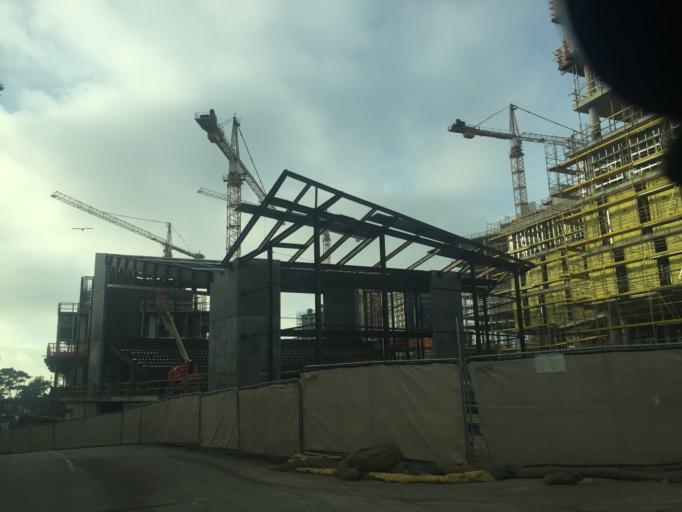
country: US
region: California
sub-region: San Diego County
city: La Jolla
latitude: 32.8798
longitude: -117.2407
